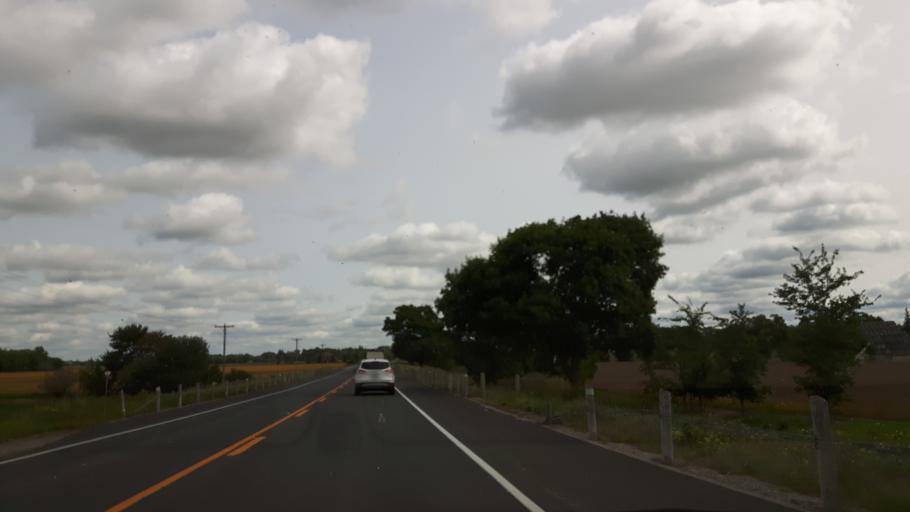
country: CA
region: Ontario
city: Huron East
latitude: 43.5643
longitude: -81.4180
